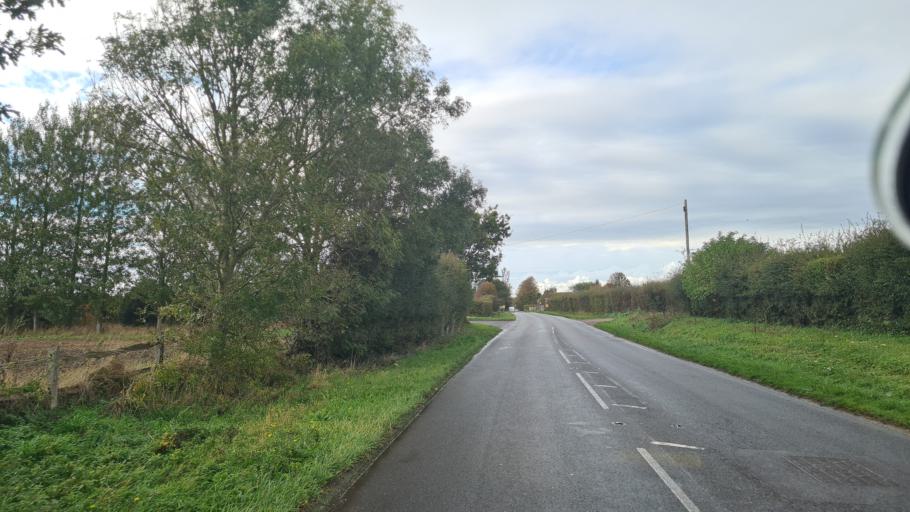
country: GB
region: England
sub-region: West Sussex
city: Walberton
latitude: 50.8137
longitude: -0.5962
